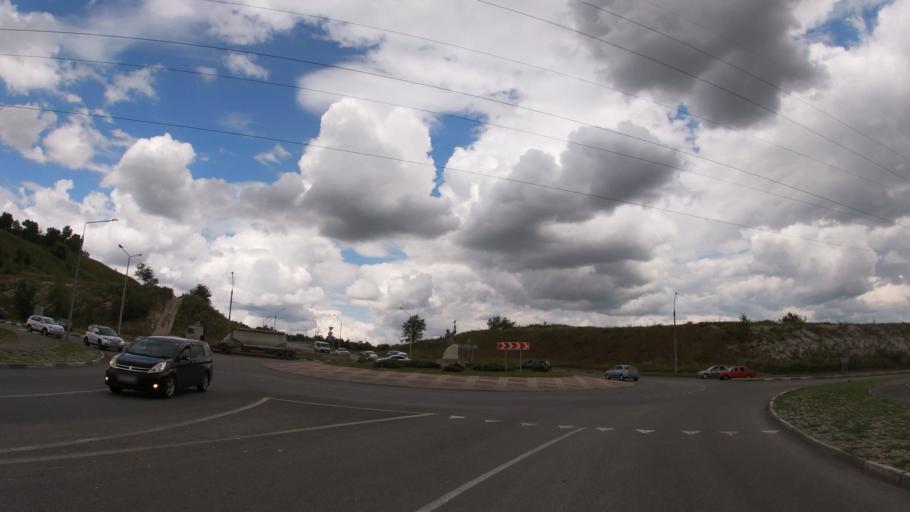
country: RU
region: Belgorod
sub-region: Belgorodskiy Rayon
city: Belgorod
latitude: 50.6171
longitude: 36.6160
